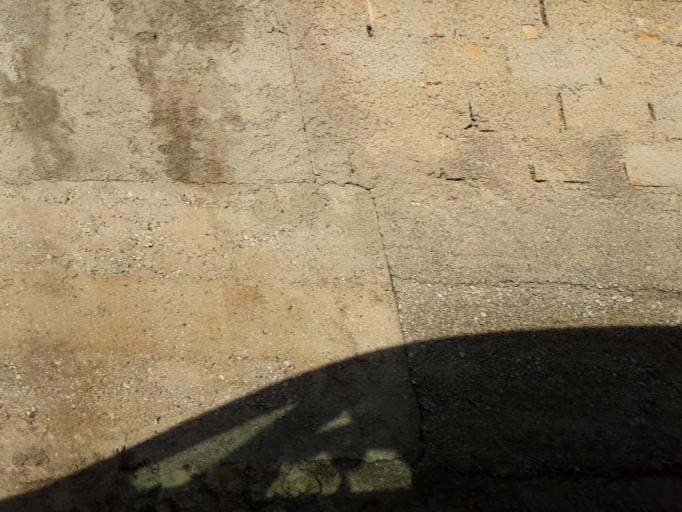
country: IT
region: Veneto
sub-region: Provincia di Treviso
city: Vittorio Veneto
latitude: 45.9697
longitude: 12.2991
